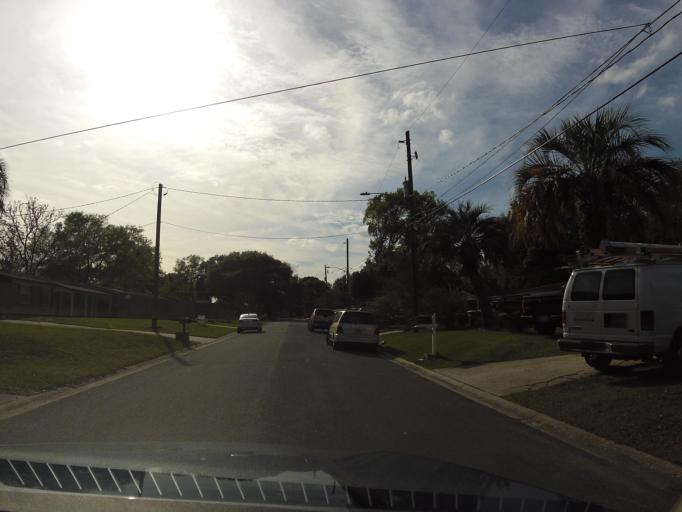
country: US
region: Florida
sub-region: Clay County
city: Bellair-Meadowbrook Terrace
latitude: 30.2420
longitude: -81.7702
